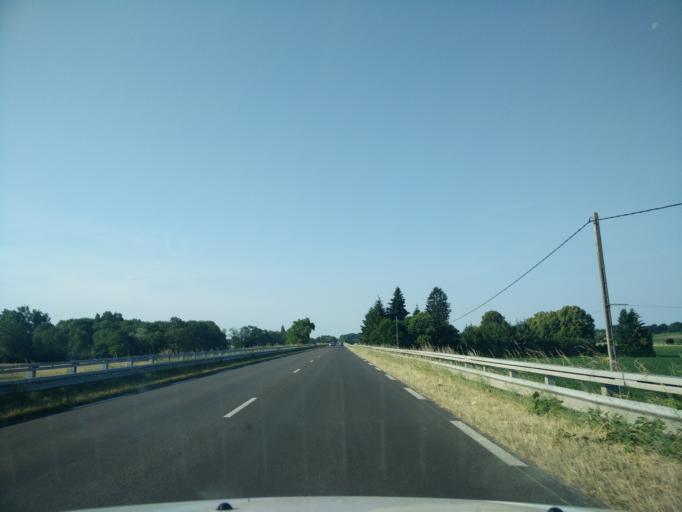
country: FR
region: Auvergne
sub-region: Departement de l'Allier
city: Moulins
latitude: 46.5516
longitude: 3.3207
